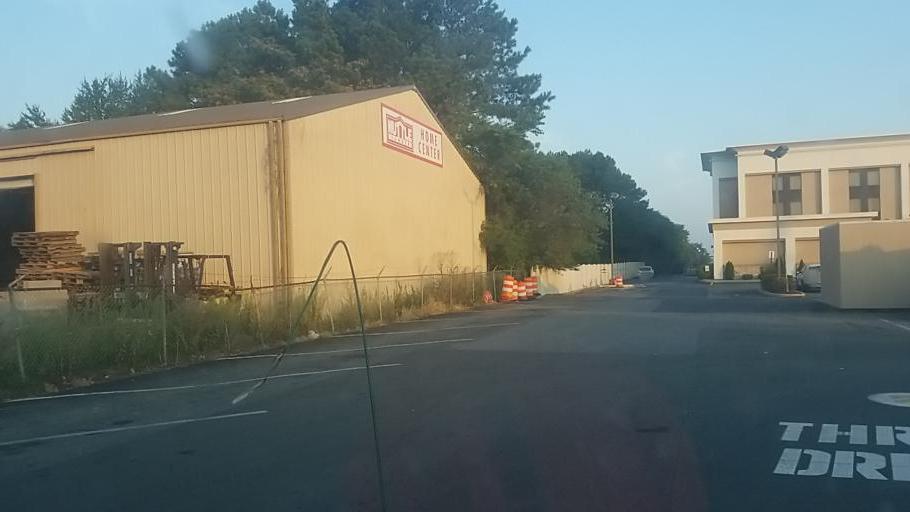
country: US
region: Delaware
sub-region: Sussex County
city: Lewes
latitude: 38.7315
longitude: -75.1352
